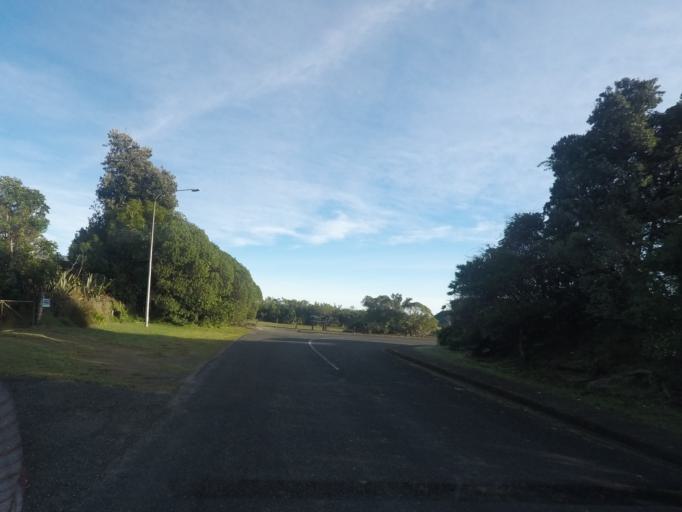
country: NZ
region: Tasman
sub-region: Tasman District
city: Takaka
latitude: -40.8113
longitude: 172.9163
